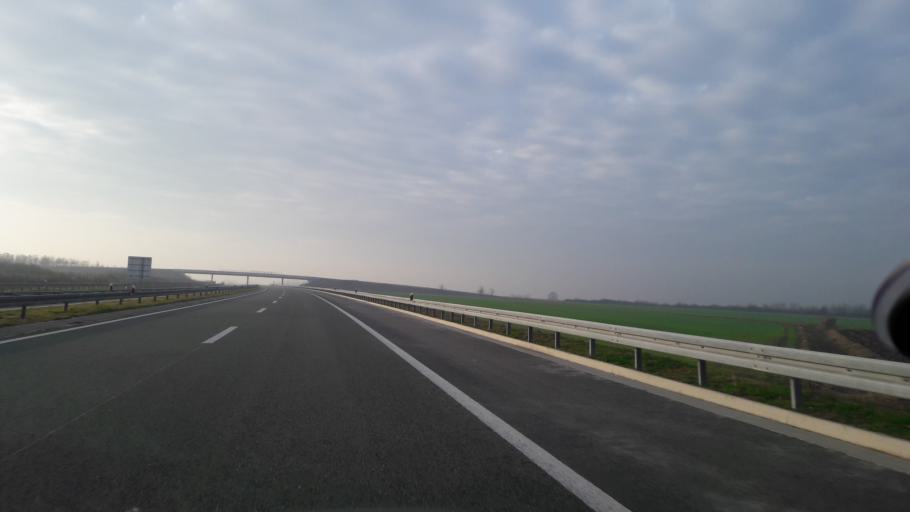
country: HR
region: Osjecko-Baranjska
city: Gorjani
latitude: 45.3826
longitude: 18.3960
